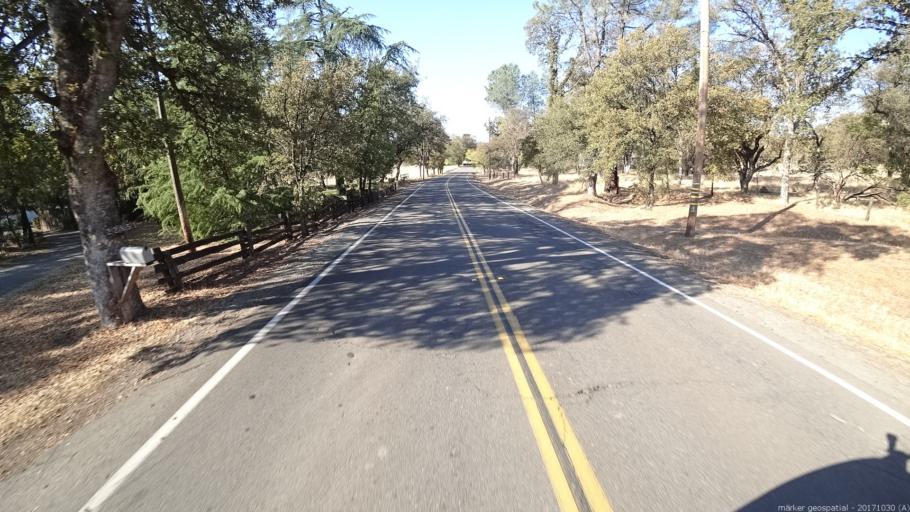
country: US
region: California
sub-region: Shasta County
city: Palo Cedro
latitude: 40.5666
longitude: -122.2070
